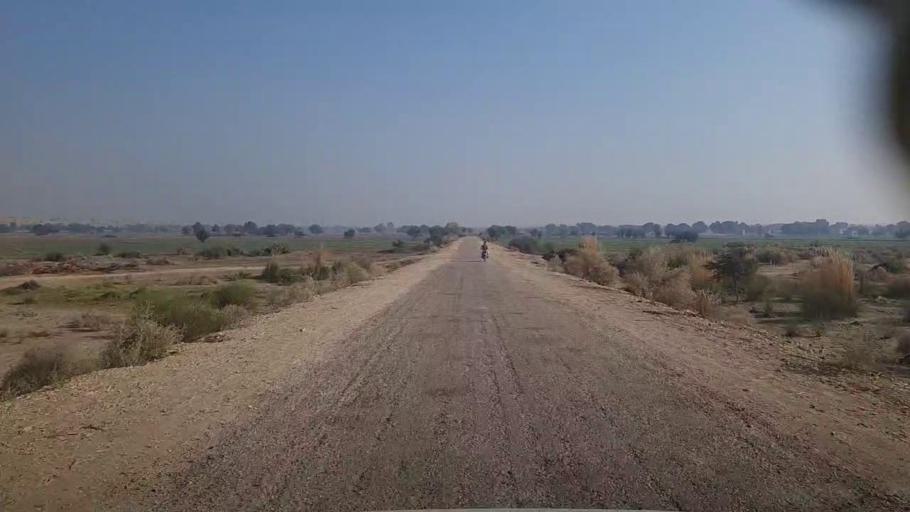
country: PK
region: Sindh
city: Kandiari
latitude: 26.8214
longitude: 68.4914
